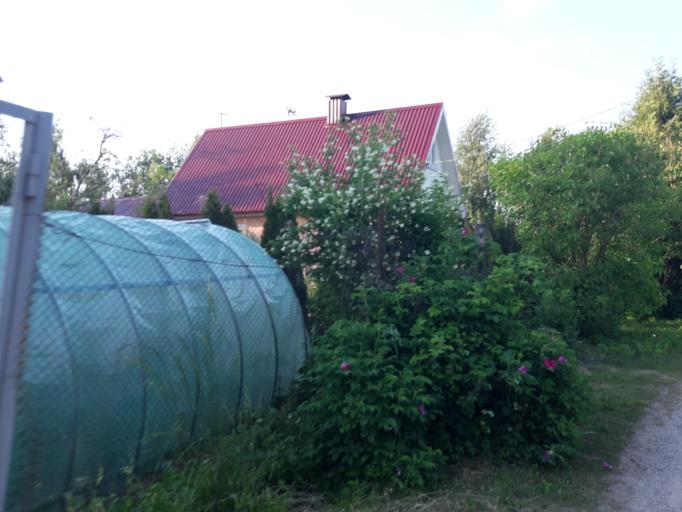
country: BY
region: Minsk
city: Pyatryshki
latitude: 54.1329
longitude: 27.1380
